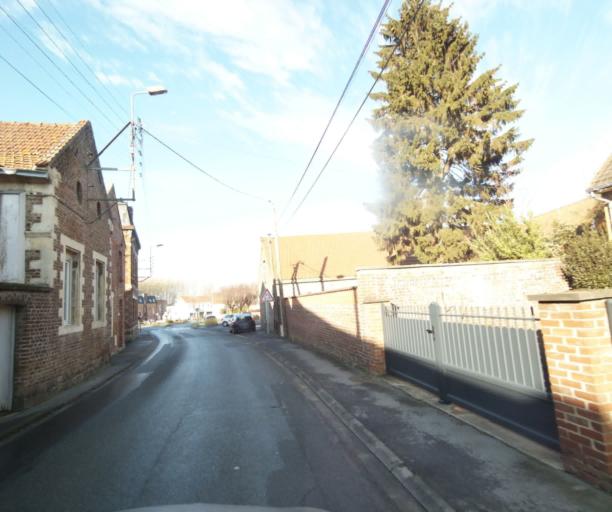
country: FR
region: Nord-Pas-de-Calais
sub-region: Departement du Nord
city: Maing
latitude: 50.3082
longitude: 3.4857
